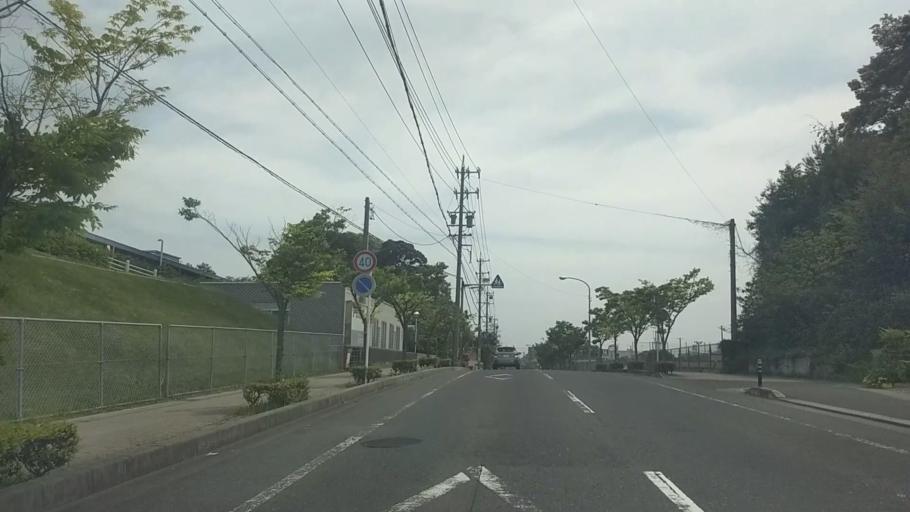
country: JP
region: Shizuoka
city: Kosai-shi
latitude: 34.7148
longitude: 137.5374
